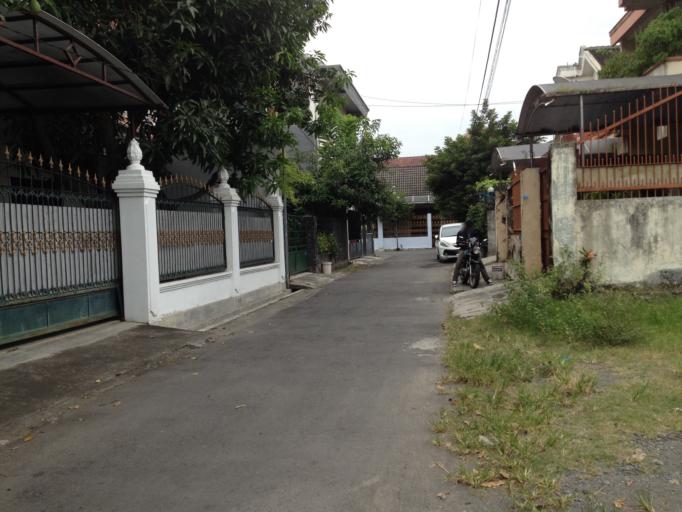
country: ID
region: Daerah Istimewa Yogyakarta
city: Yogyakarta
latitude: -7.8238
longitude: 110.3765
